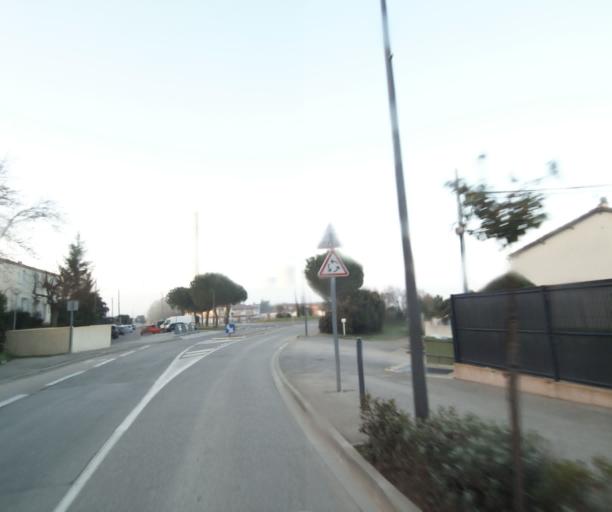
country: FR
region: Provence-Alpes-Cote d'Azur
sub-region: Departement des Bouches-du-Rhone
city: Meyreuil
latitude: 43.4785
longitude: 5.4923
